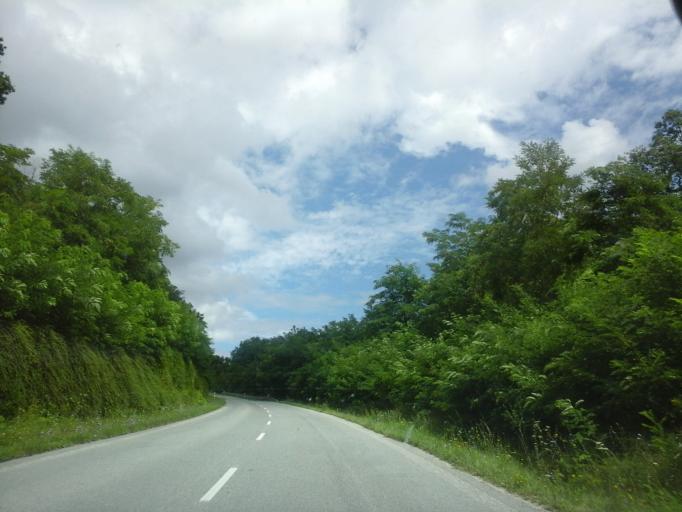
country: SK
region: Kosicky
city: Roznava
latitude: 48.5291
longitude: 20.4092
